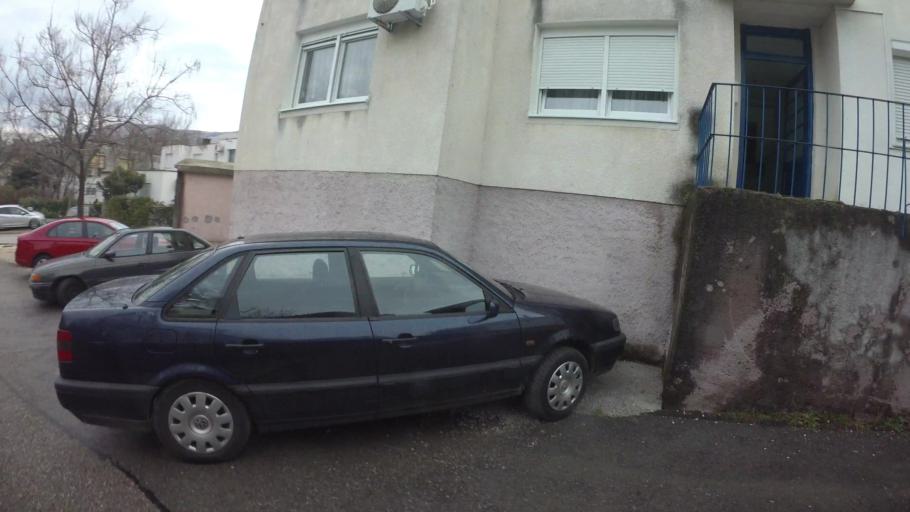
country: BA
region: Federation of Bosnia and Herzegovina
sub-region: Hercegovacko-Bosanski Kanton
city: Mostar
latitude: 43.3349
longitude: 17.7975
